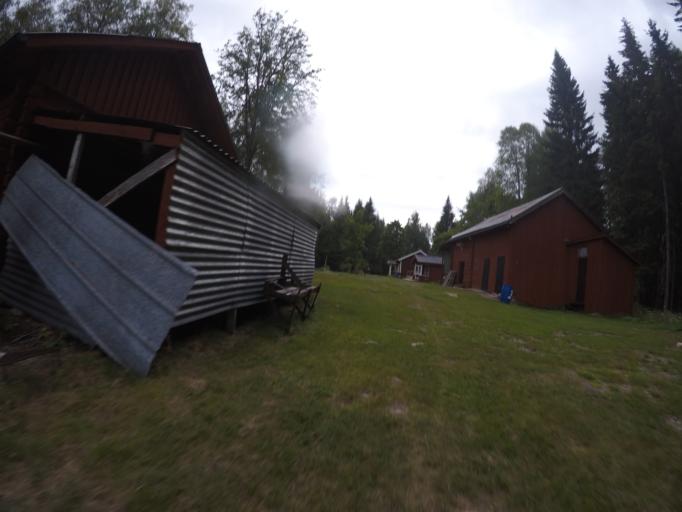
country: SE
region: OErebro
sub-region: Hallefors Kommun
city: Haellefors
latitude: 60.0392
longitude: 14.5149
